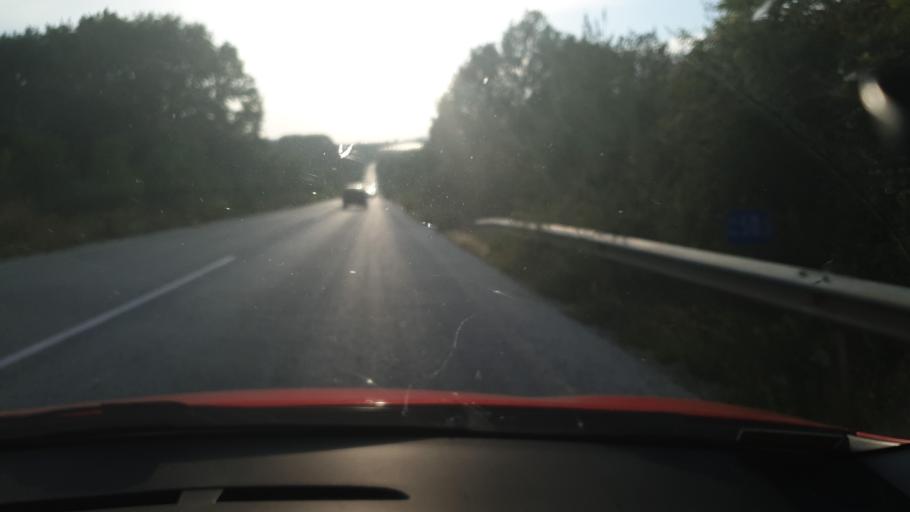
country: GR
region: Central Macedonia
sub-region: Nomos Chalkidikis
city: Polygyros
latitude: 40.4614
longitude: 23.3912
